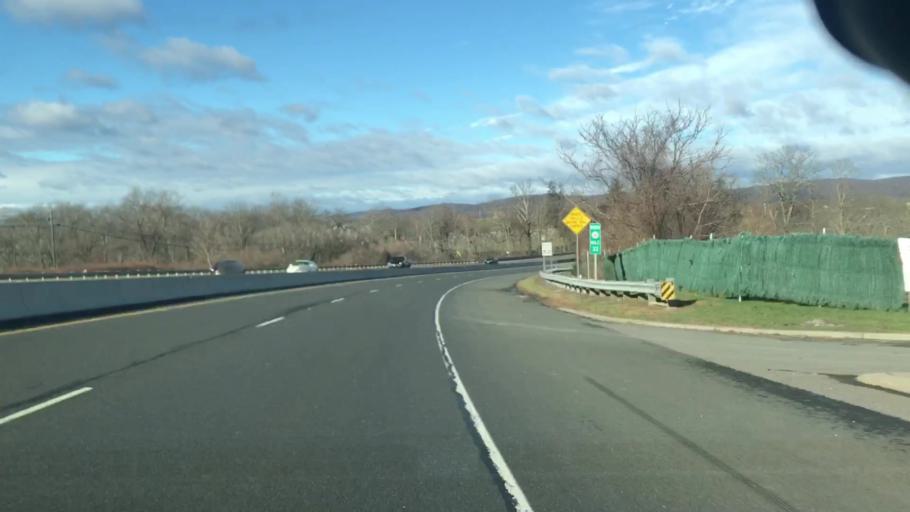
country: US
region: New Jersey
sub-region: Hunterdon County
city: Clinton
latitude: 40.6432
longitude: -74.9070
